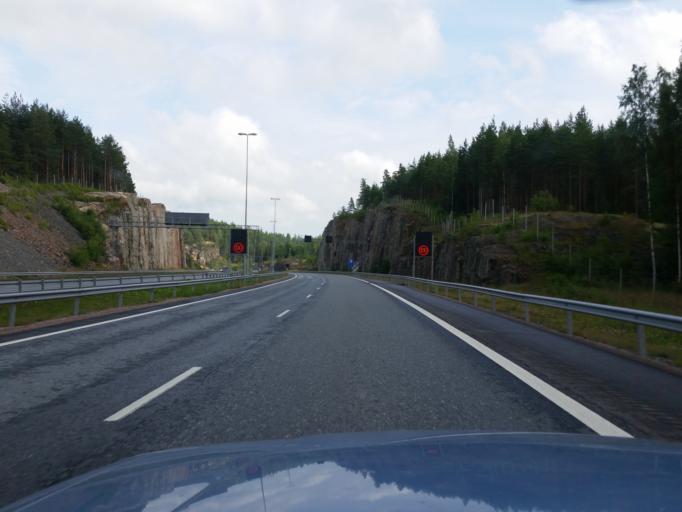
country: FI
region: Uusimaa
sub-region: Helsinki
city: Saukkola
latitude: 60.3167
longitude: 23.9708
